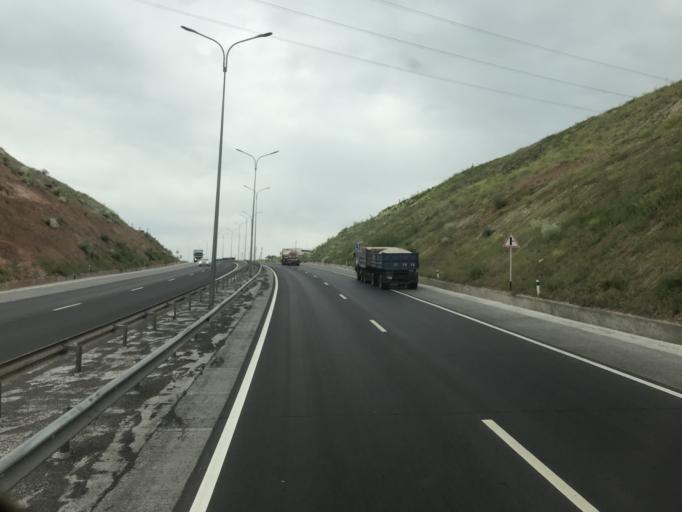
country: KZ
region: Ongtustik Qazaqstan
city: Qazyqurt
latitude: 41.9983
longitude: 69.4761
